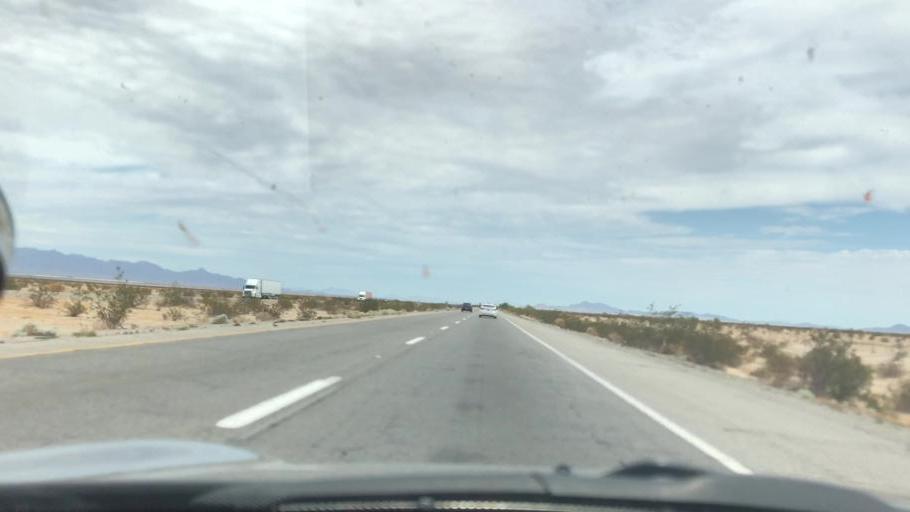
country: US
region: California
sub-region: Riverside County
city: Mesa Verde
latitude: 33.6429
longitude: -115.1101
